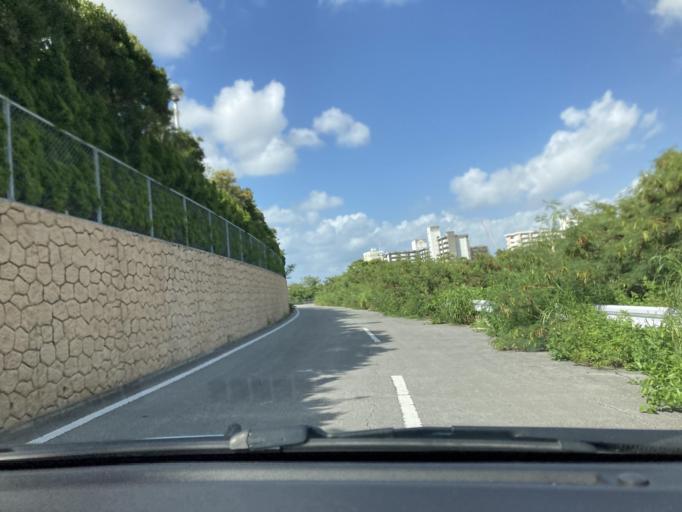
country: JP
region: Okinawa
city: Tomigusuku
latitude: 26.1887
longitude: 127.6865
